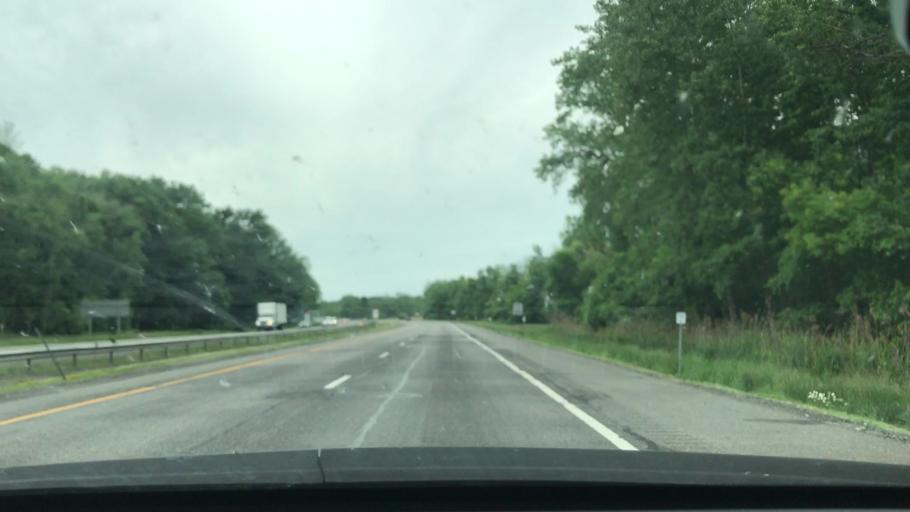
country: US
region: New York
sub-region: Onondaga County
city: Liverpool
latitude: 43.1182
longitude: -76.2306
